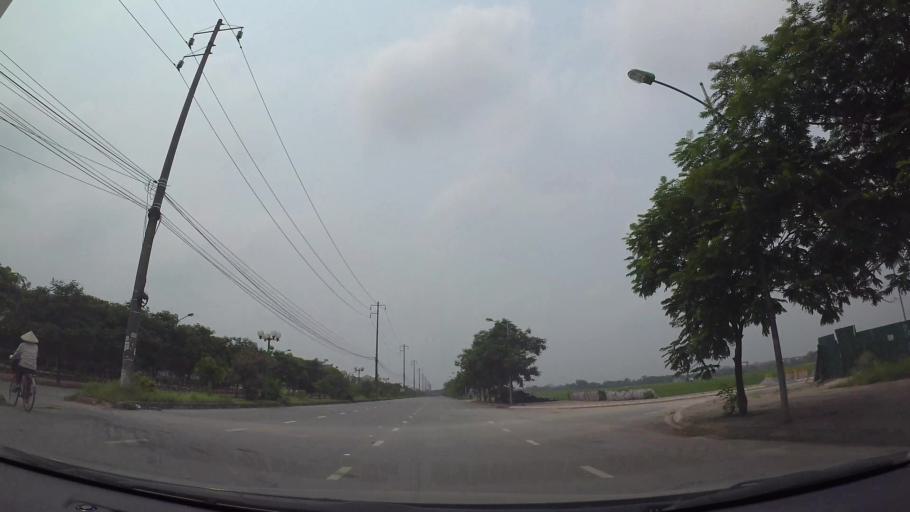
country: VN
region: Ha Noi
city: Trau Quy
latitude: 21.0649
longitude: 105.9121
